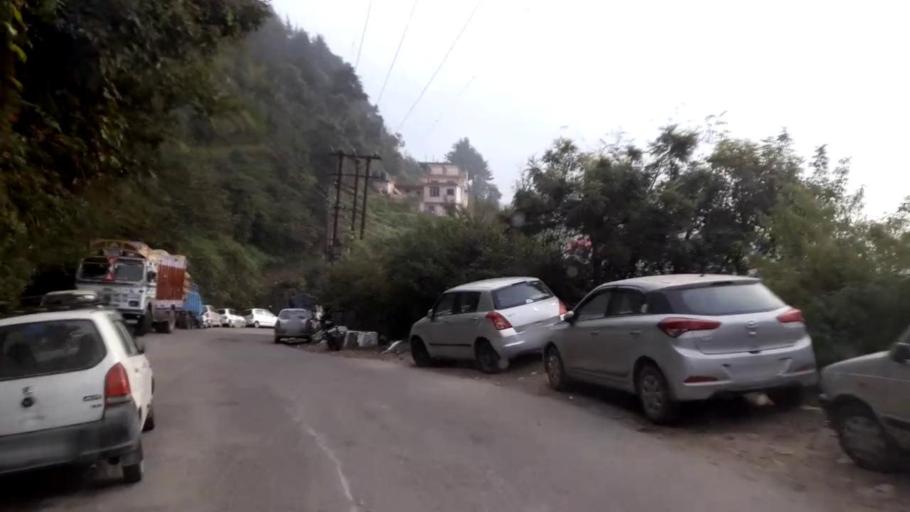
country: IN
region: Himachal Pradesh
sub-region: Shimla
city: Jutogh
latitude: 31.0426
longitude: 77.1276
